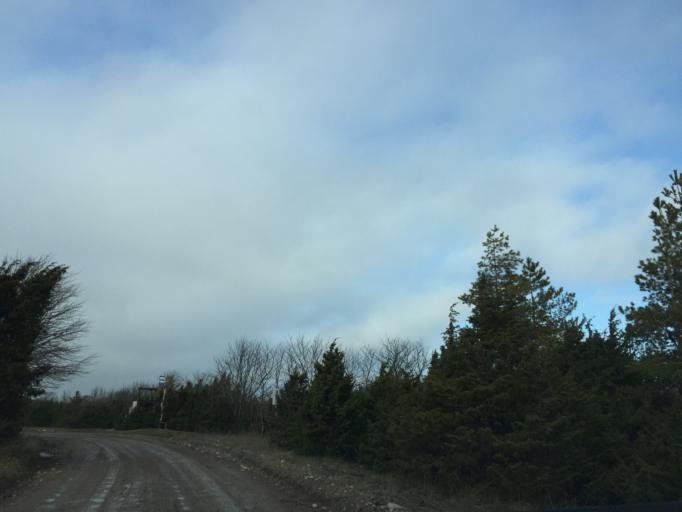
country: EE
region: Saare
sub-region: Kuressaare linn
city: Kuressaare
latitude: 58.4938
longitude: 21.9325
